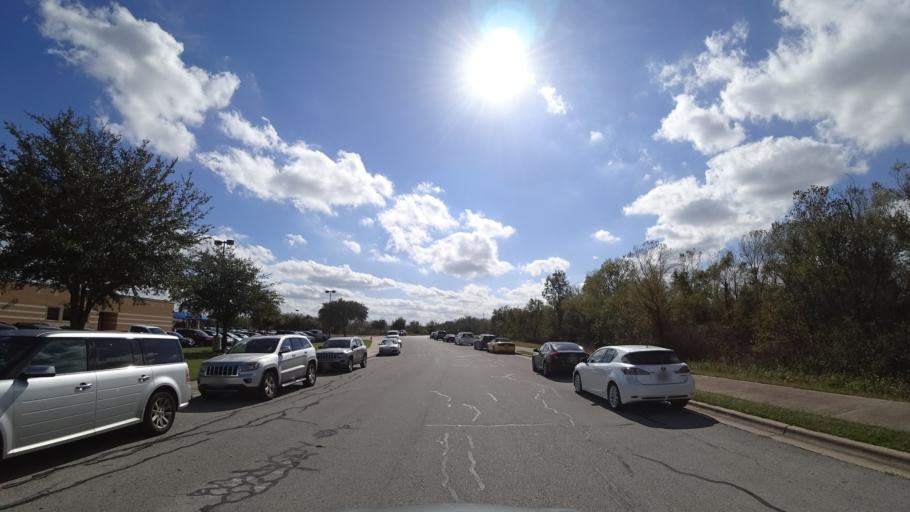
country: US
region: Texas
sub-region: Travis County
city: Windemere
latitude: 30.4692
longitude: -97.6562
